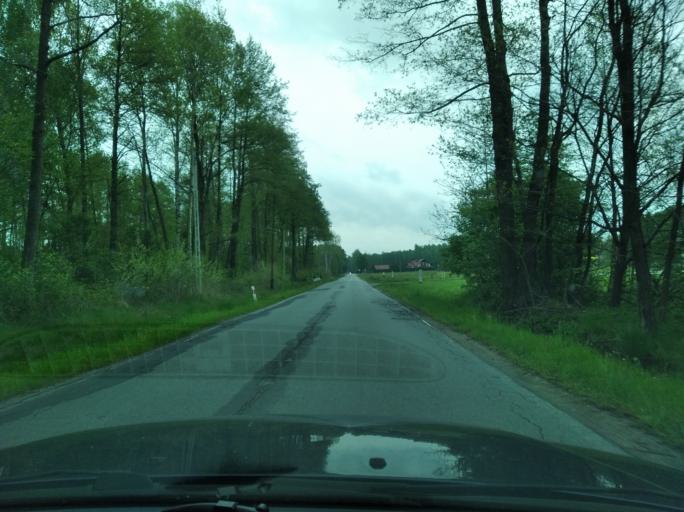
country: PL
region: Subcarpathian Voivodeship
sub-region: Powiat kolbuszowski
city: Kolbuszowa
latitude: 50.1888
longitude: 21.7629
